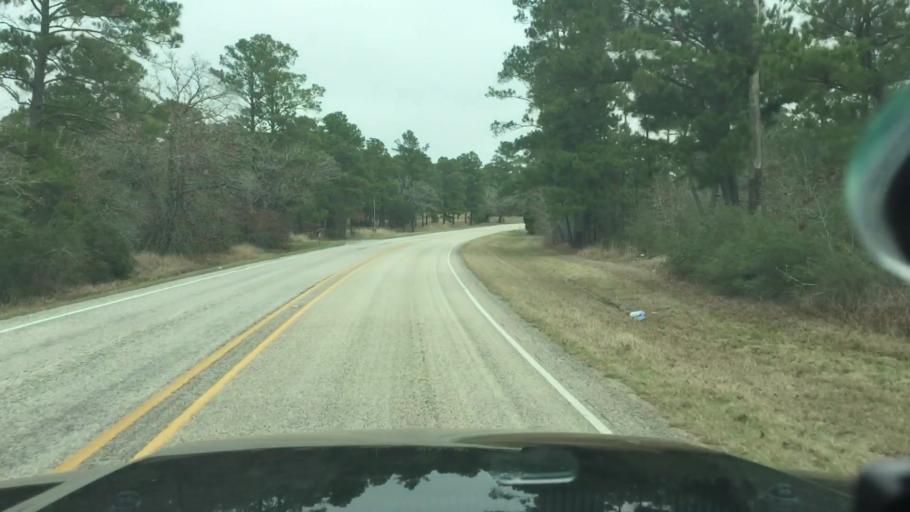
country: US
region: Texas
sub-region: Fayette County
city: La Grange
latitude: 30.0090
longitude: -96.9425
